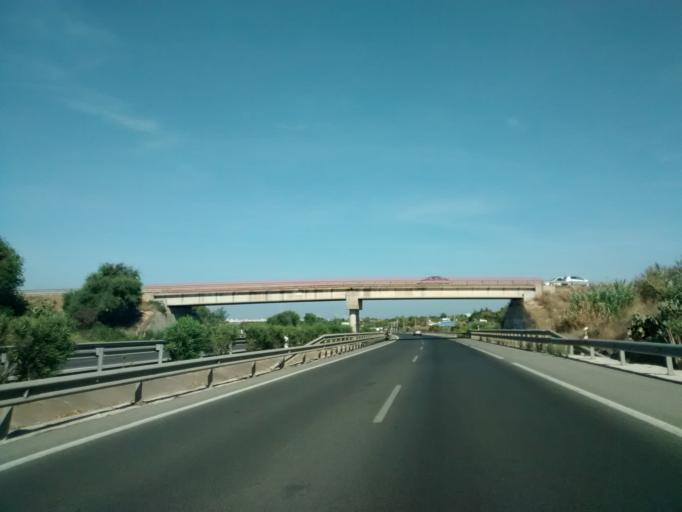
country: ES
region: Andalusia
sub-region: Provincia de Cadiz
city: Chiclana de la Frontera
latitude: 36.4366
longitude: -6.1229
